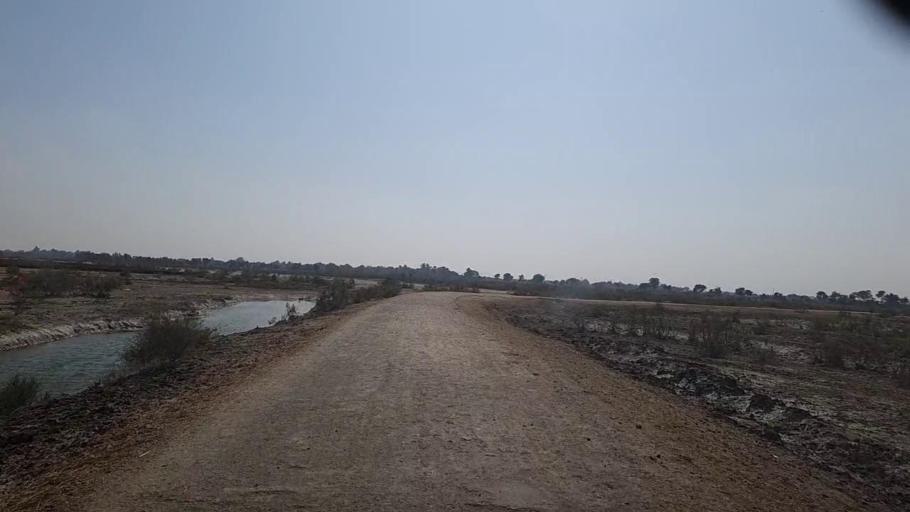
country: PK
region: Sindh
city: Thul
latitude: 28.1742
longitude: 68.7723
